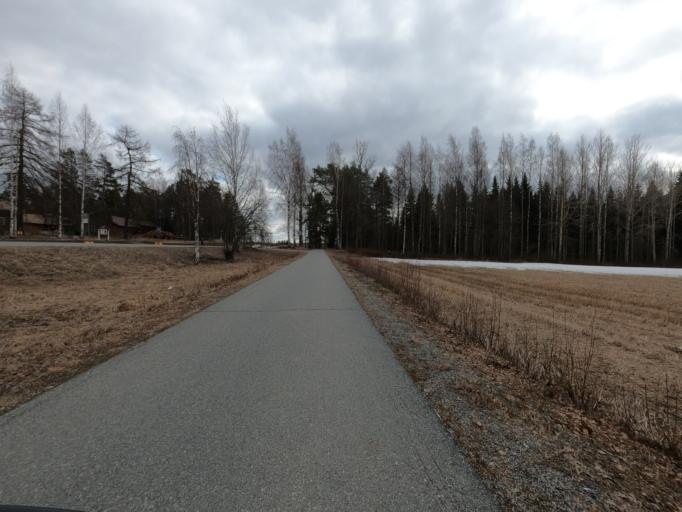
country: FI
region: North Karelia
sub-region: Joensuu
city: Joensuu
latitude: 62.5617
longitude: 29.8145
